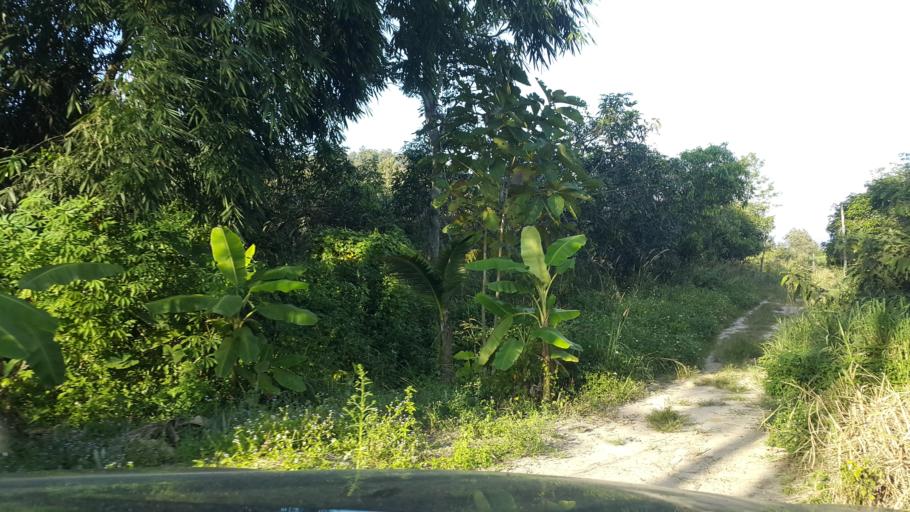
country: TH
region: Chiang Mai
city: San Kamphaeng
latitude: 18.7092
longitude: 99.1961
